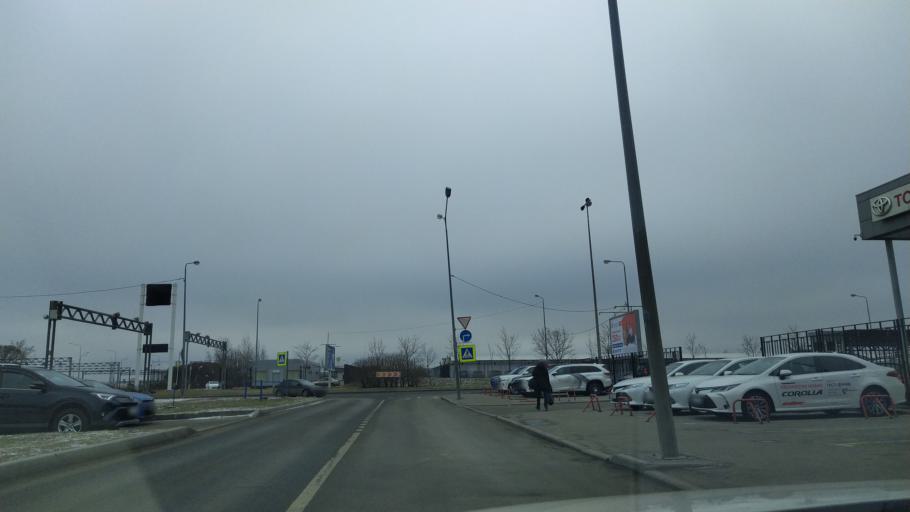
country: RU
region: St.-Petersburg
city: Kupchino
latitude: 59.8050
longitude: 30.3220
